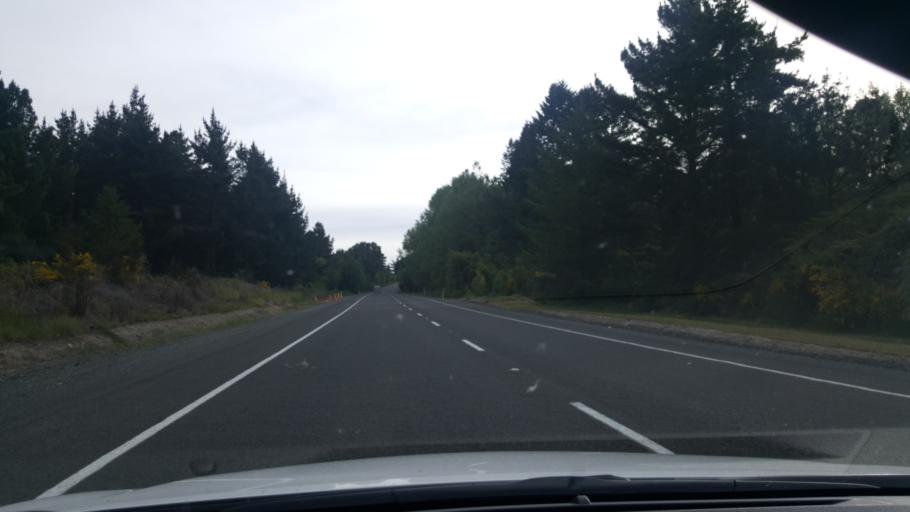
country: NZ
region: Waikato
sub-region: Taupo District
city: Taupo
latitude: -38.6168
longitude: 176.1113
